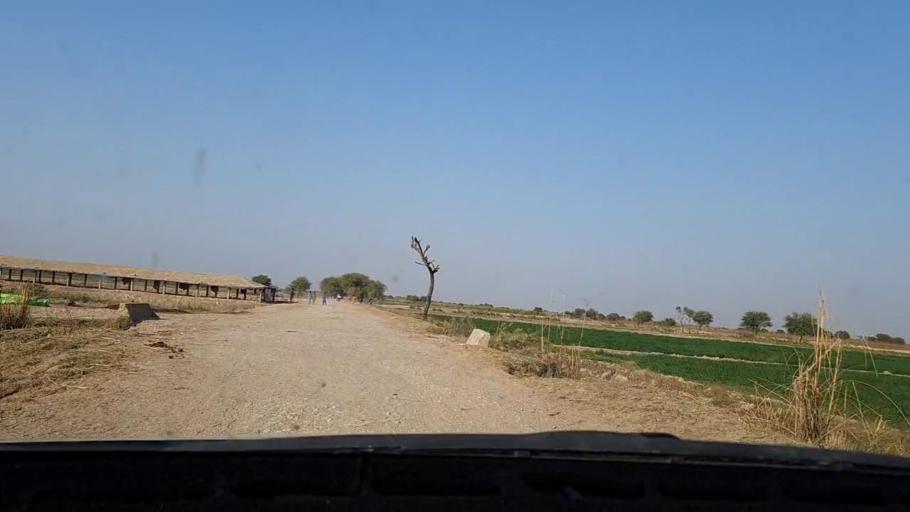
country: PK
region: Sindh
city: Tando Mittha Khan
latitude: 25.8427
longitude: 69.3326
